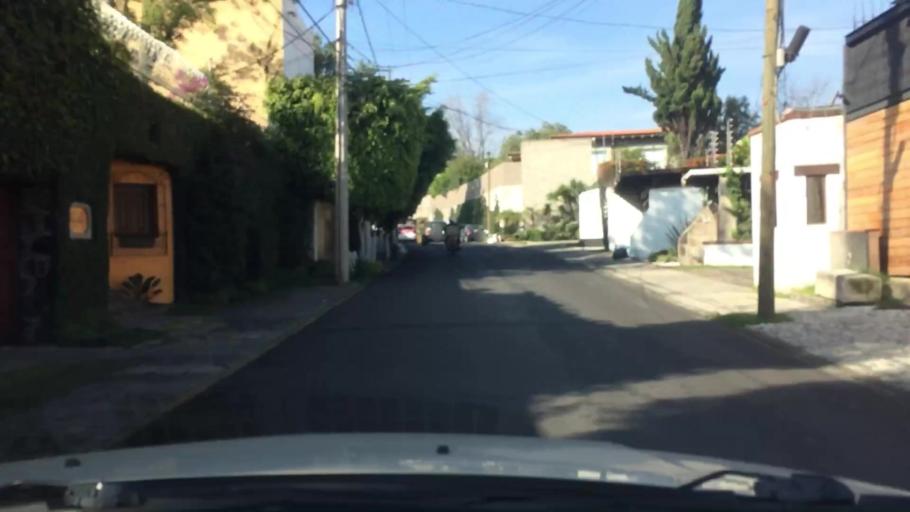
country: MX
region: Mexico City
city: Magdalena Contreras
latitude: 19.3220
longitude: -99.2066
